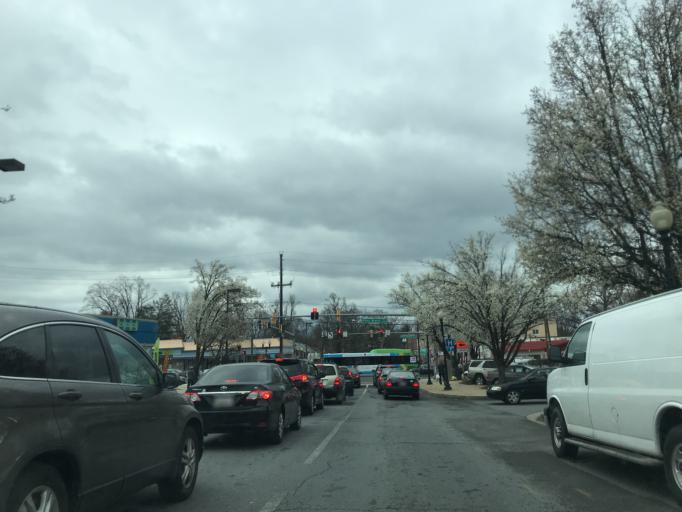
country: US
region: Maryland
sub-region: Montgomery County
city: Takoma Park
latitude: 38.9989
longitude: -77.0038
